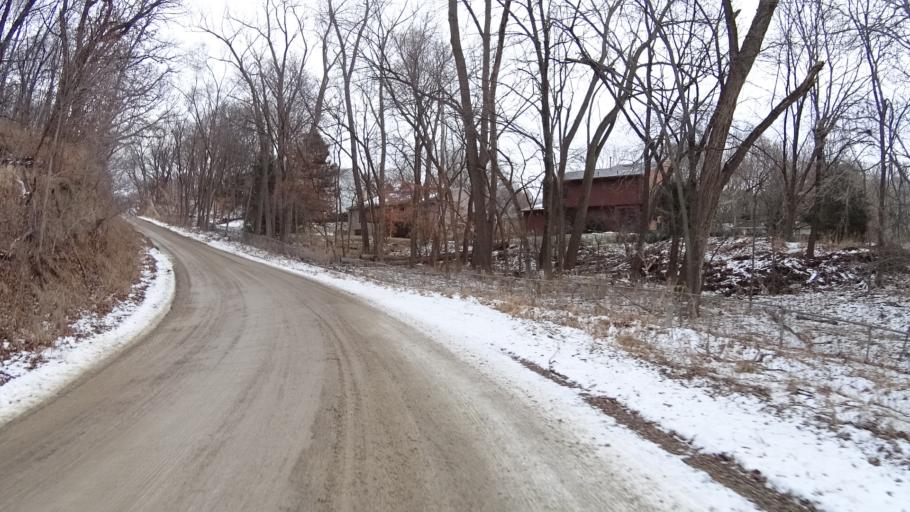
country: US
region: Nebraska
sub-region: Sarpy County
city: Bellevue
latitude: 41.1693
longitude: -95.9036
